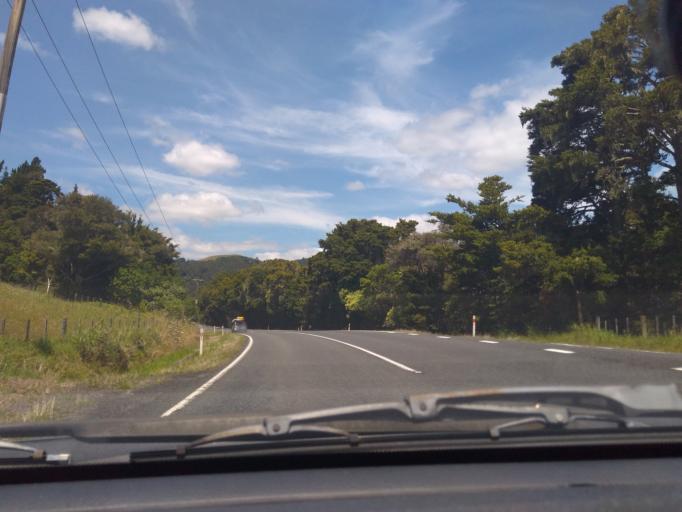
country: NZ
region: Northland
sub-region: Far North District
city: Kerikeri
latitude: -35.1124
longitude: 173.8070
